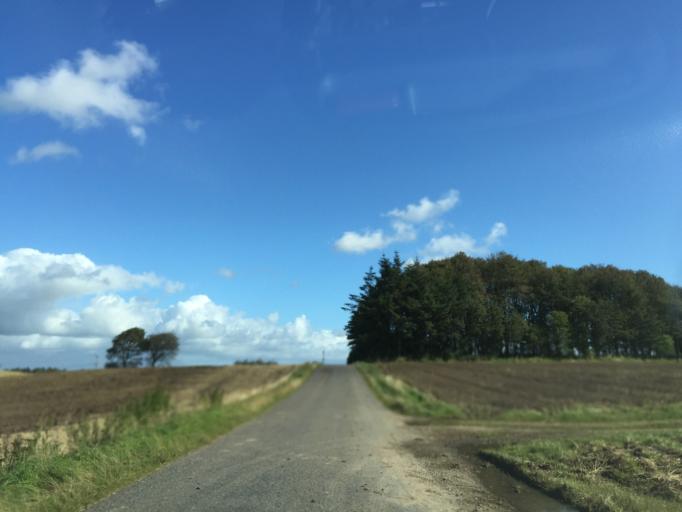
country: DK
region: Central Jutland
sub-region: Viborg Kommune
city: Bjerringbro
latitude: 56.4142
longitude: 9.5649
